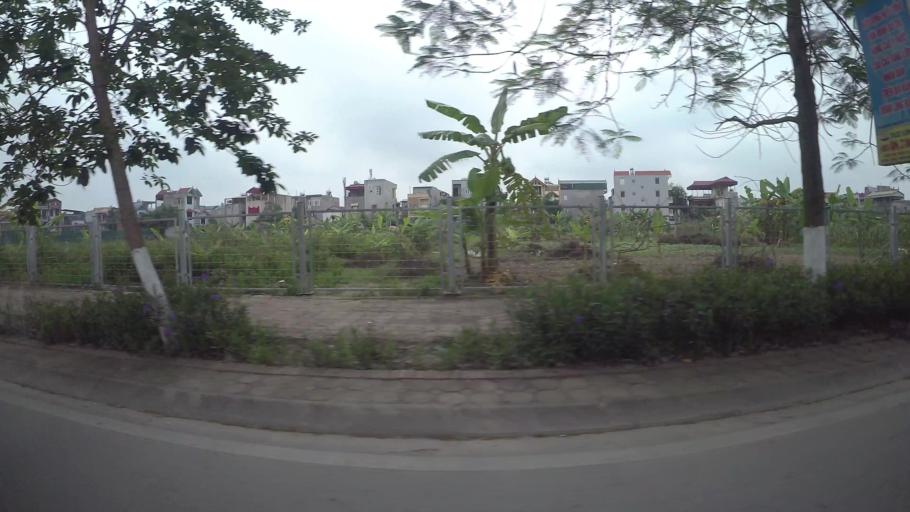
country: VN
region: Ha Noi
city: Trau Quy
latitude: 21.0520
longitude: 105.9210
